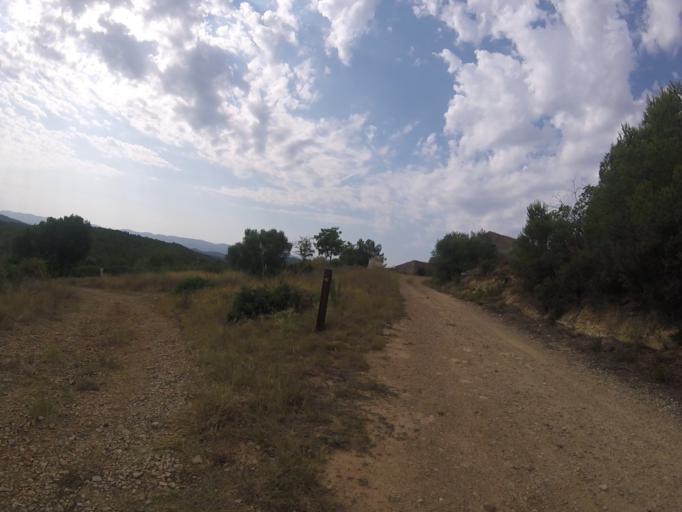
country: ES
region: Valencia
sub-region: Provincia de Castello
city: Alcala de Xivert
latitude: 40.3814
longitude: 0.2070
